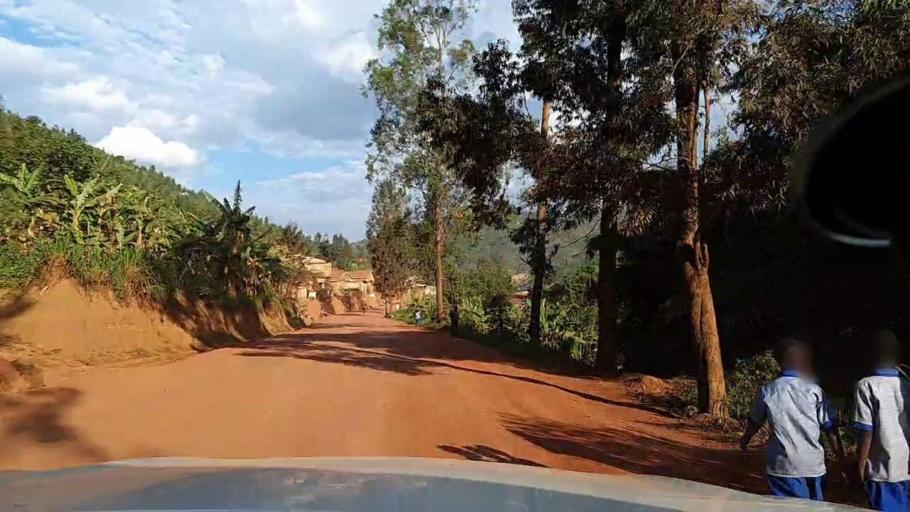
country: RW
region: Kigali
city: Kigali
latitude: -1.9463
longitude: 30.0127
